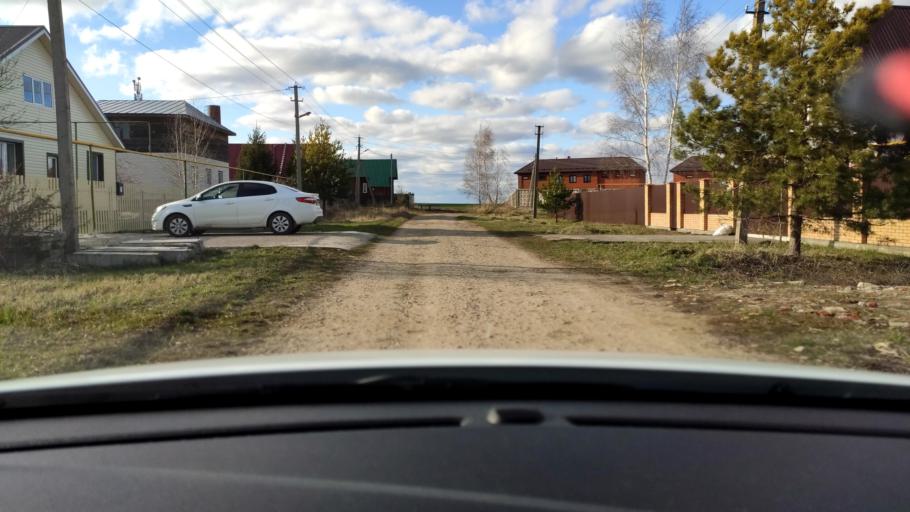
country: RU
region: Tatarstan
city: Vysokaya Gora
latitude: 55.8911
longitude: 49.3585
